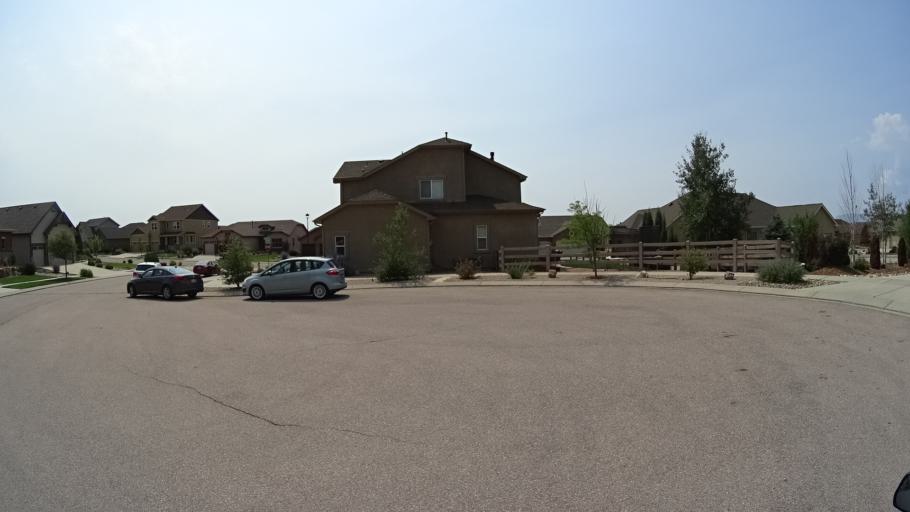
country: US
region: Colorado
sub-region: El Paso County
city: Black Forest
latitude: 38.9678
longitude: -104.7177
